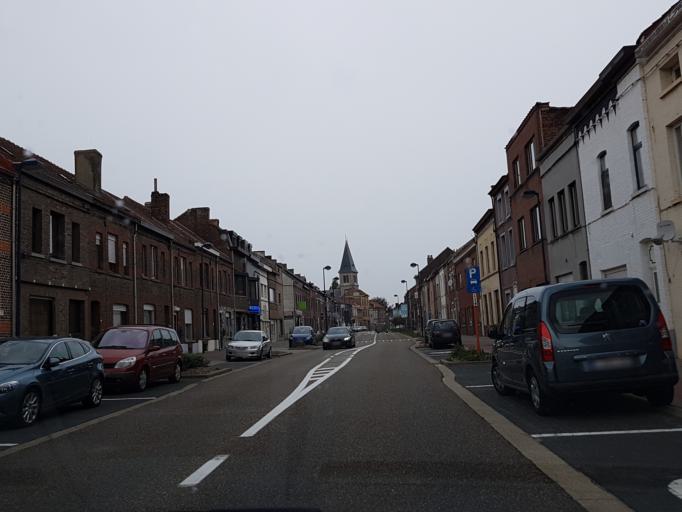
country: BE
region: Flanders
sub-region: Provincie Vlaams-Brabant
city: Tienen
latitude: 50.8007
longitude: 4.9573
